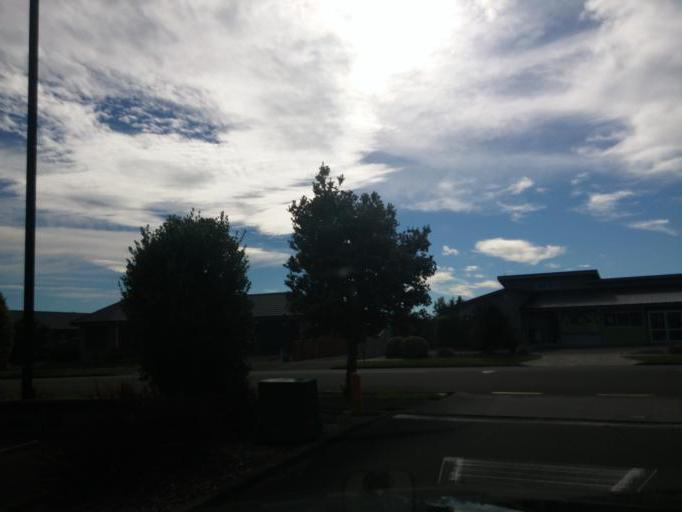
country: NZ
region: Manawatu-Wanganui
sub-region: Palmerston North City
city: Palmerston North
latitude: -40.3870
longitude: 175.6391
